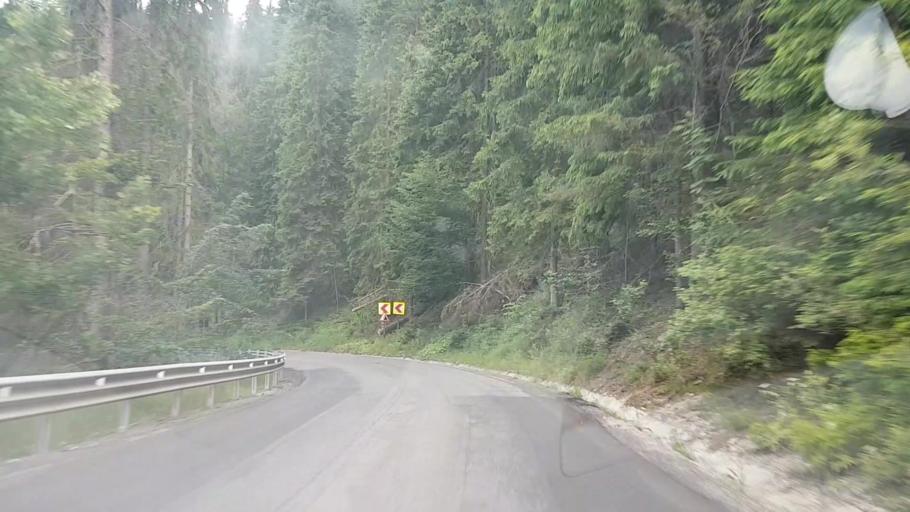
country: RO
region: Harghita
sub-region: Comuna Varsag
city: Varsag
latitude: 46.6425
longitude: 25.2821
